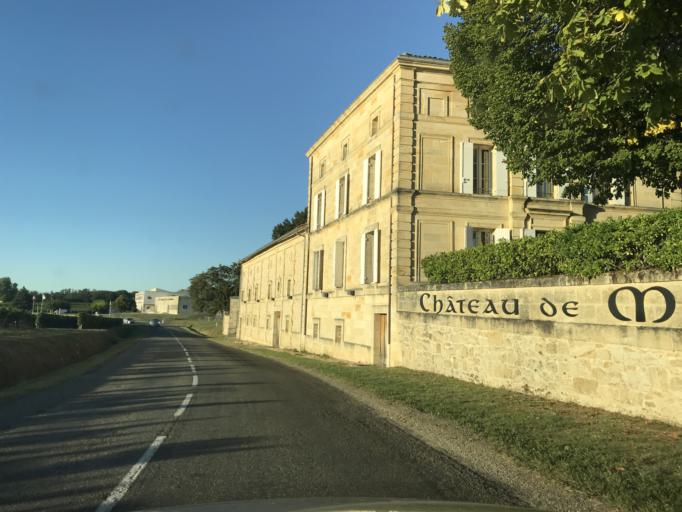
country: FR
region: Aquitaine
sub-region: Departement de la Gironde
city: Lussac
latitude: 44.9341
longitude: -0.0715
